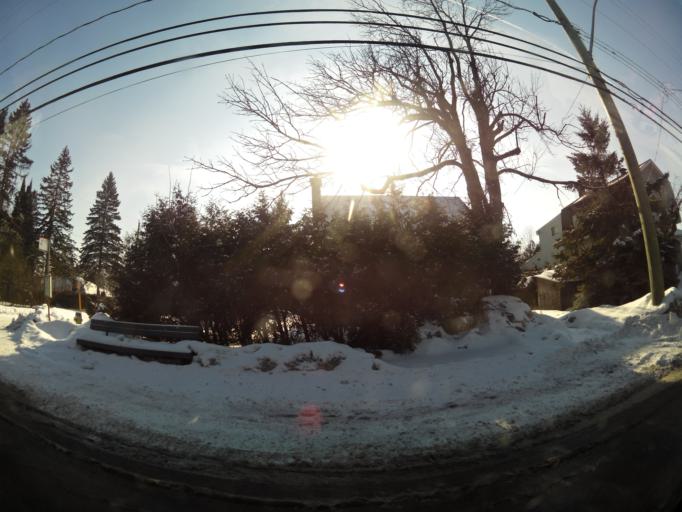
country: CA
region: Ontario
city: Ottawa
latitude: 45.3870
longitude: -75.6571
